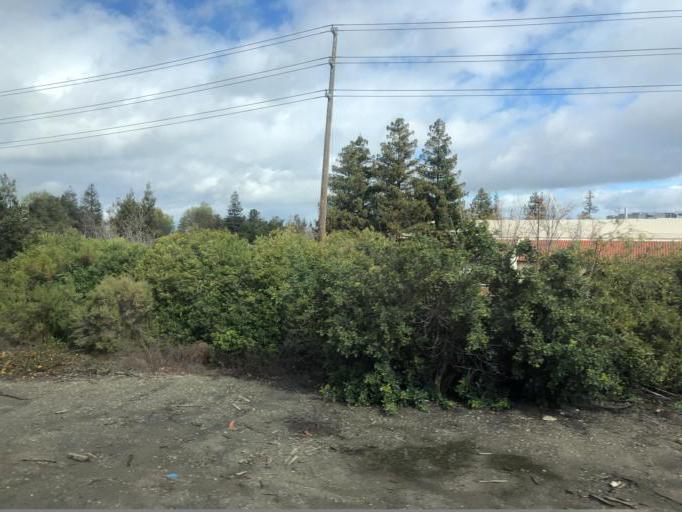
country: US
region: California
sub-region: Santa Clara County
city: Santa Clara
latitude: 37.3700
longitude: -121.9749
